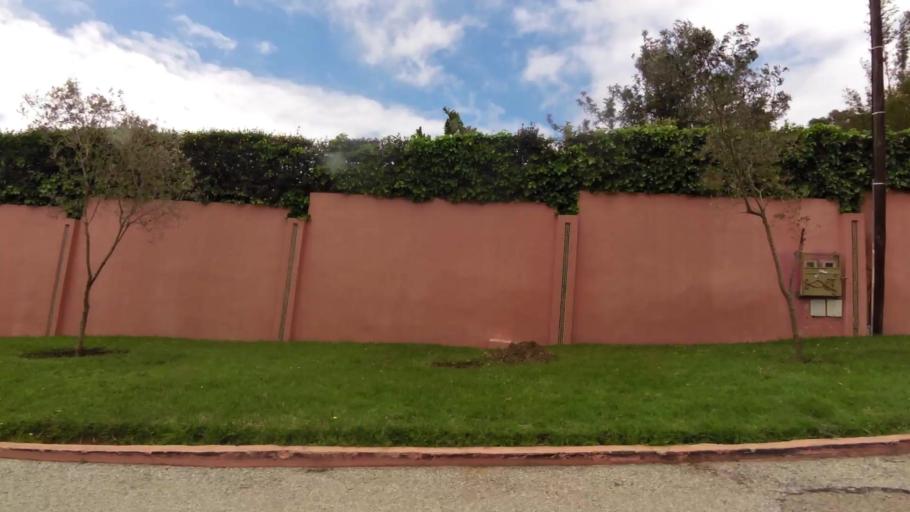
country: MA
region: Tanger-Tetouan
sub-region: Tanger-Assilah
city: Tangier
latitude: 35.7839
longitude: -5.8498
